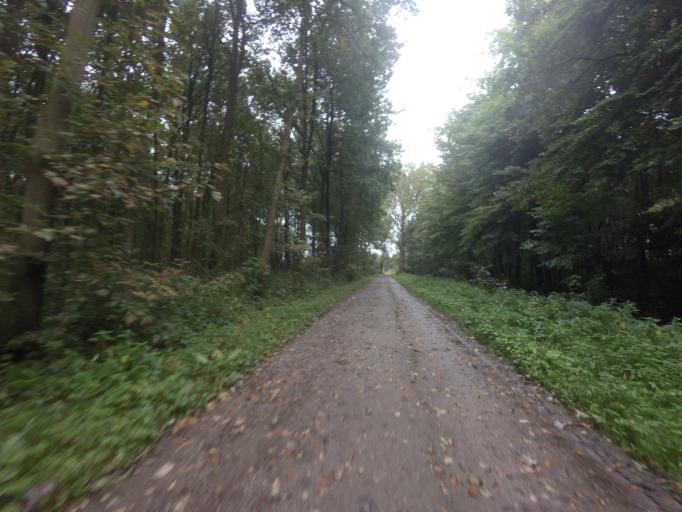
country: NL
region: South Holland
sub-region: Gemeente Papendrecht
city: Papendrecht
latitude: 51.8531
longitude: 4.6865
